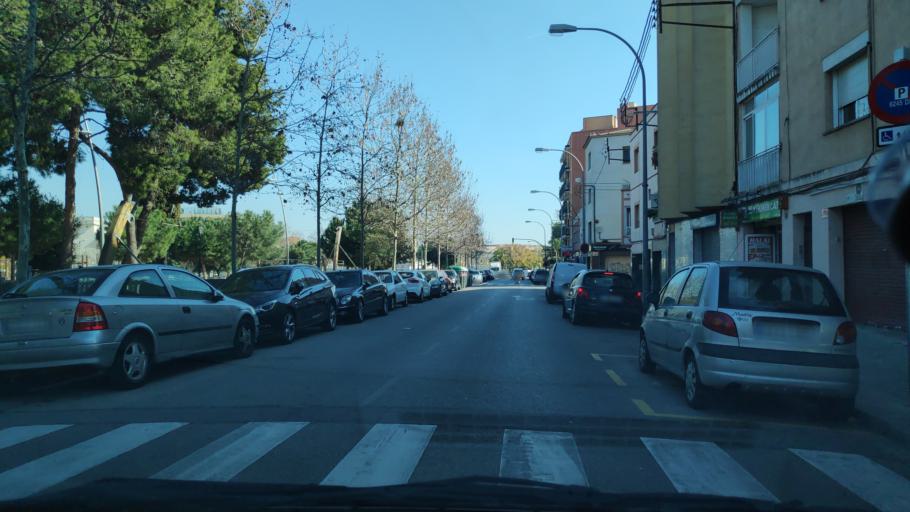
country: ES
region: Catalonia
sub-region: Provincia de Barcelona
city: Sant Quirze del Valles
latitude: 41.5466
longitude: 2.0888
